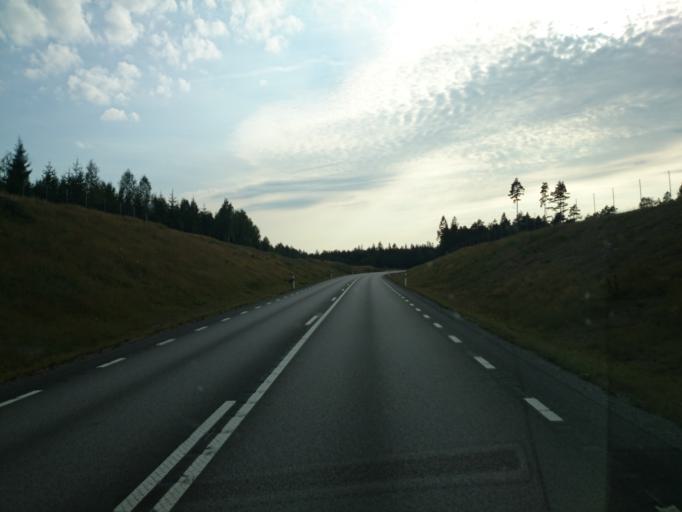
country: SE
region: Kronoberg
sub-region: Markaryds Kommun
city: Stromsnasbruk
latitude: 56.4544
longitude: 13.7527
